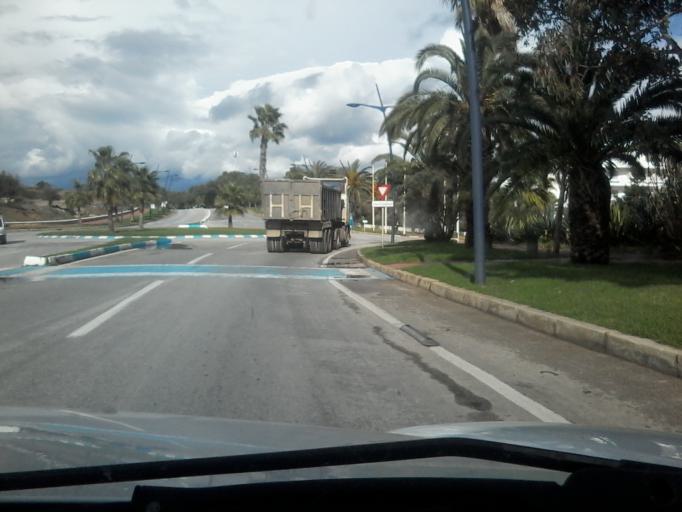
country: ES
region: Ceuta
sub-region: Ceuta
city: Ceuta
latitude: 35.7631
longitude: -5.3486
